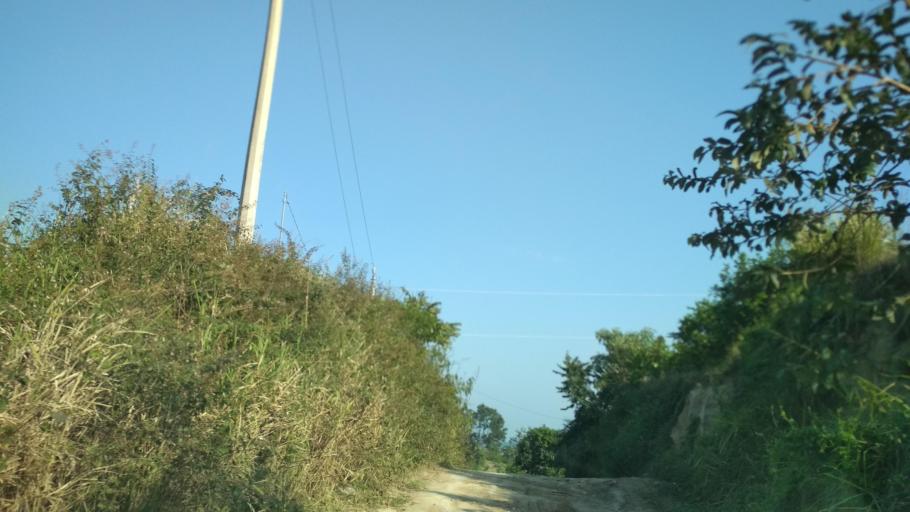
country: MX
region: Puebla
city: San Jose Acateno
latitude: 20.2196
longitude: -97.2611
